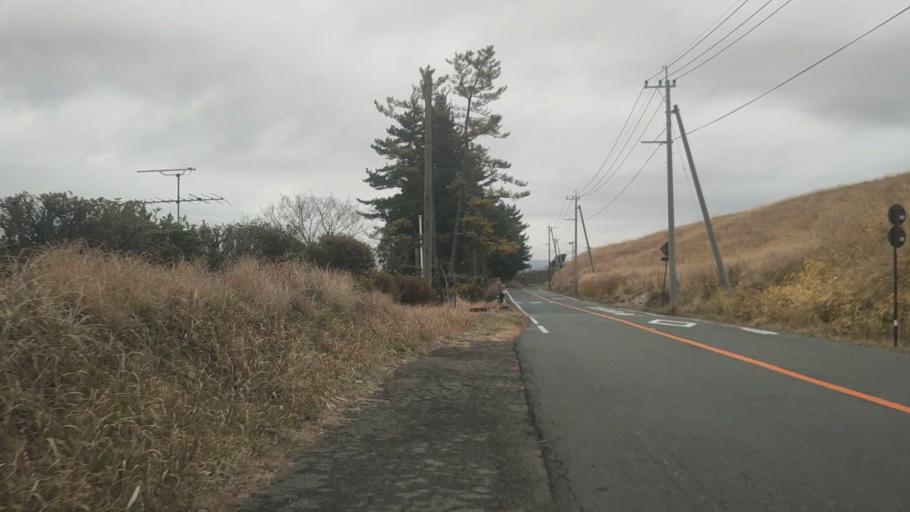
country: JP
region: Kumamoto
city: Aso
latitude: 32.8921
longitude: 131.0274
